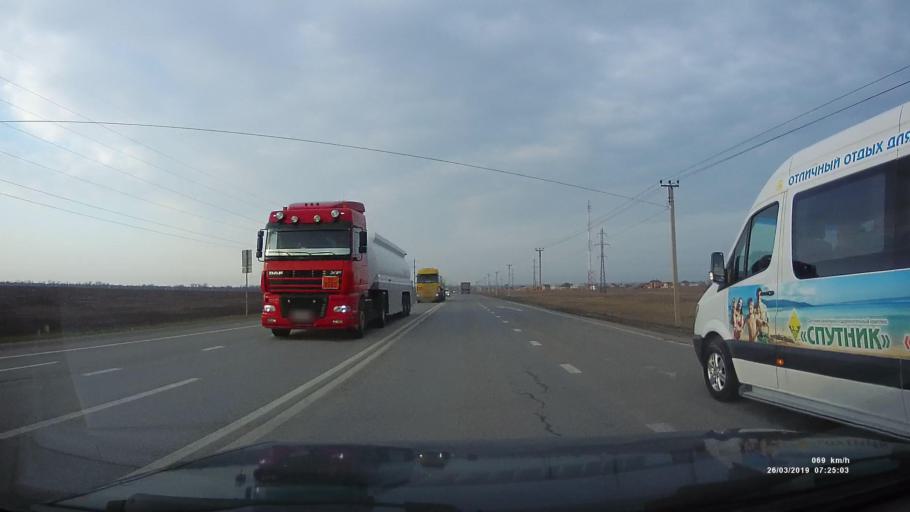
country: RU
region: Rostov
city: Taganrog
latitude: 47.2739
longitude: 38.8539
